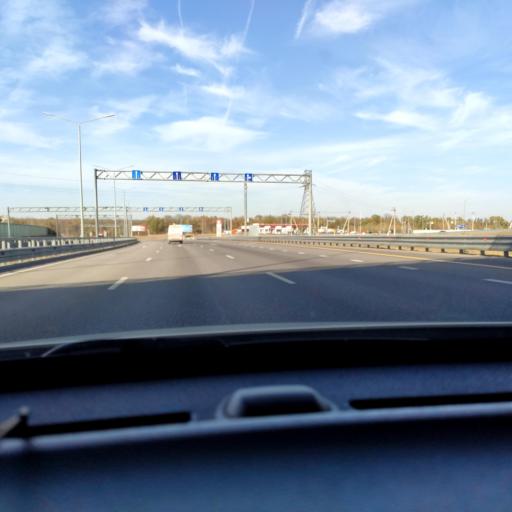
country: RU
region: Voronezj
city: Ramon'
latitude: 51.8226
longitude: 39.2505
